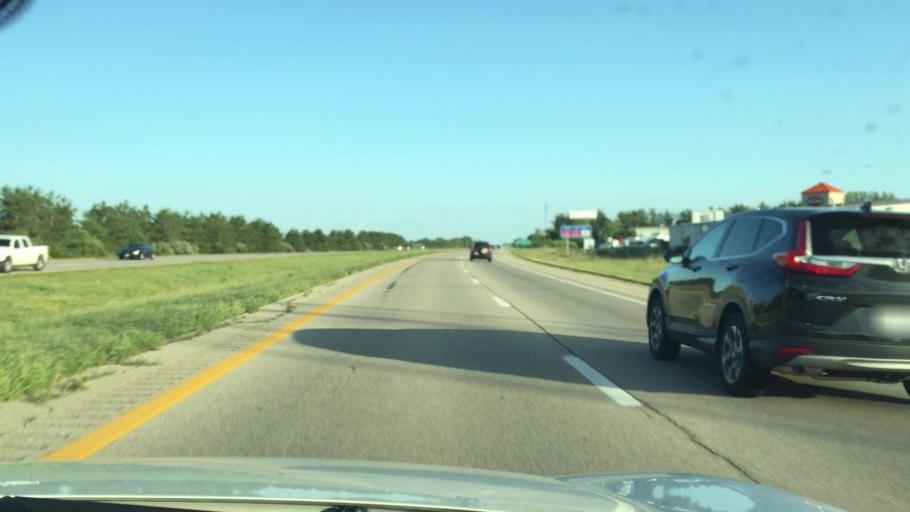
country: US
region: Ohio
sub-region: Union County
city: New California
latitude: 40.1255
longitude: -83.1880
